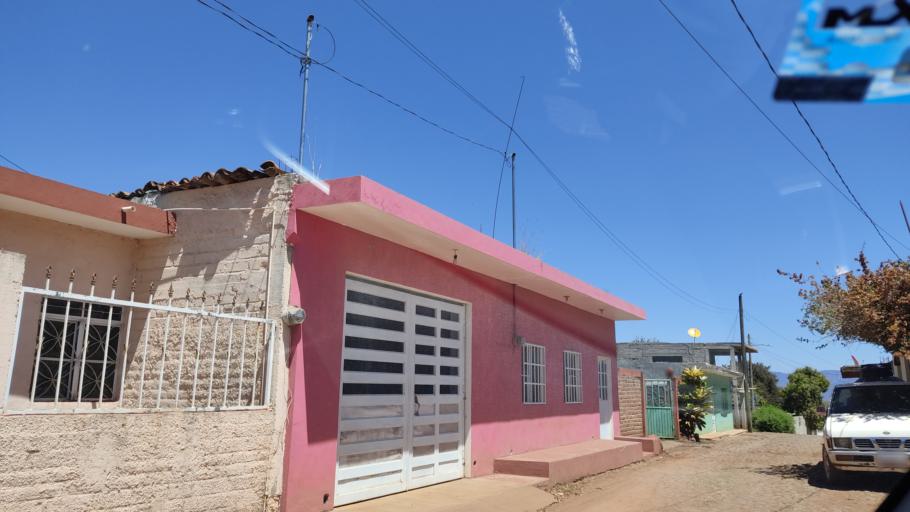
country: MX
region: Nayarit
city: Santa Maria del Oro
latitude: 21.4272
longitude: -104.6085
